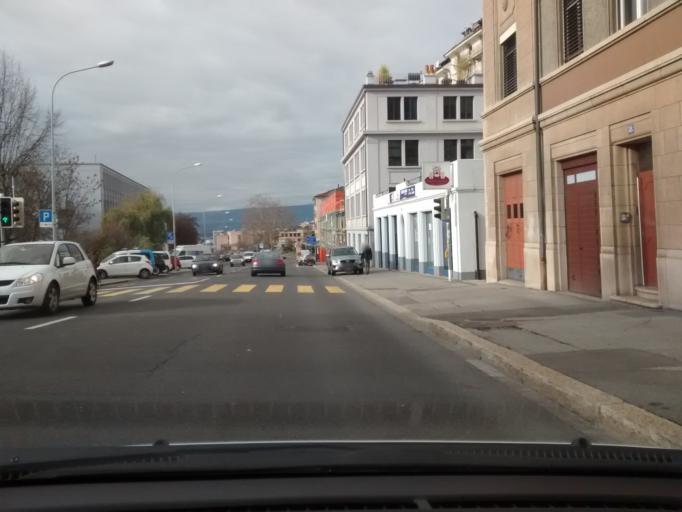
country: CH
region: Vaud
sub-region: Lausanne District
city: Lausanne
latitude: 46.5232
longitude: 6.6224
